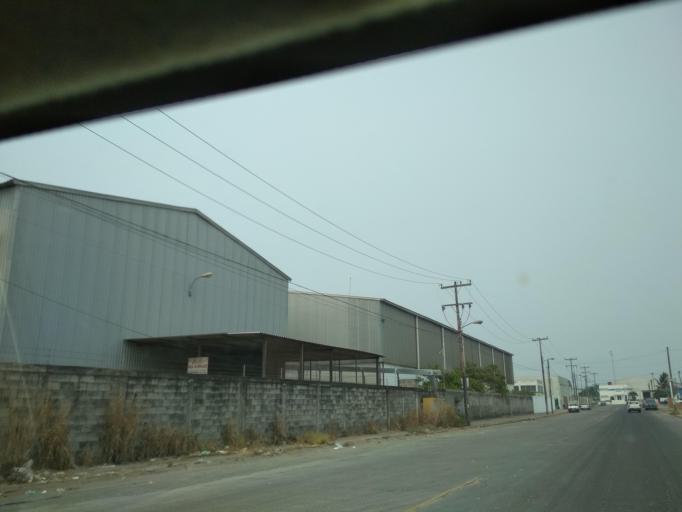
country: MX
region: Veracruz
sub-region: Veracruz
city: Las Amapolas
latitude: 19.1596
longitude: -96.2283
